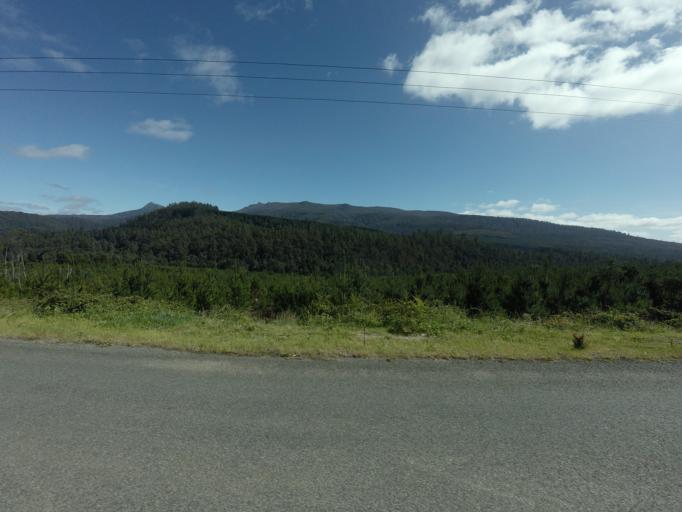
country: AU
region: Tasmania
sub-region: Derwent Valley
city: New Norfolk
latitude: -42.7459
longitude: 146.6526
